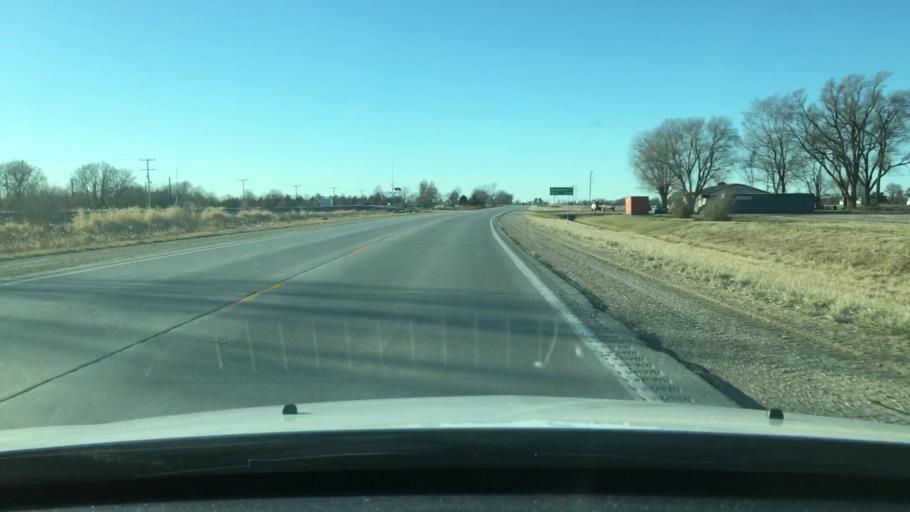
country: US
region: Missouri
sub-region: Audrain County
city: Mexico
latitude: 39.1914
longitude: -92.0087
